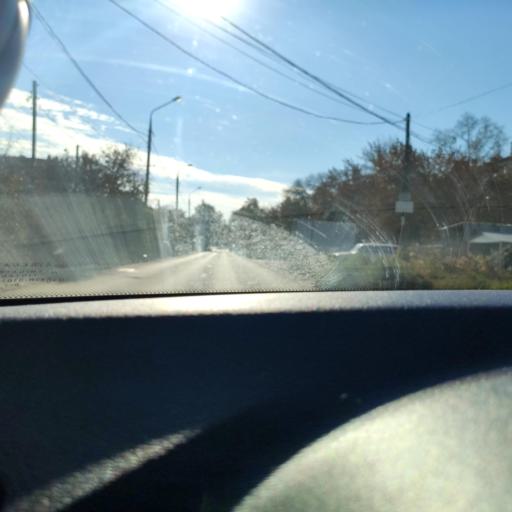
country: RU
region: Samara
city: Smyshlyayevka
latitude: 53.2315
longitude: 50.2989
